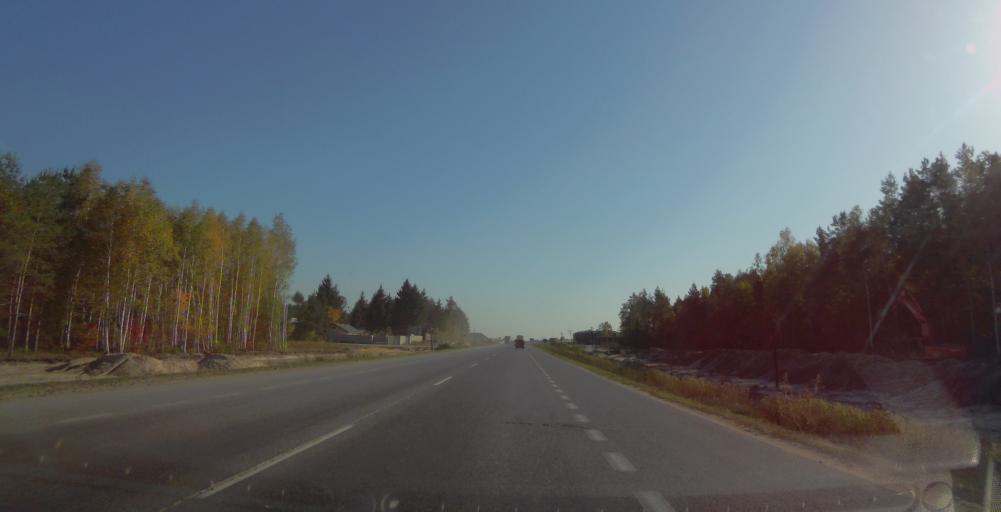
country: PL
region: Masovian Voivodeship
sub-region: Powiat minski
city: Sulejowek
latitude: 52.2126
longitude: 21.2591
